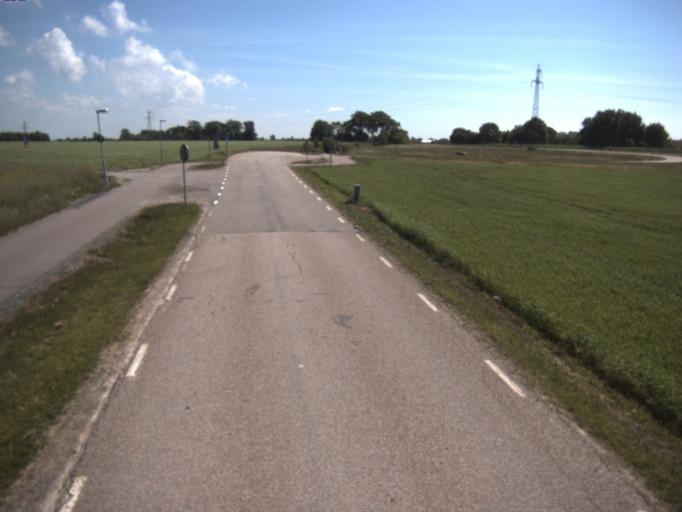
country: SE
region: Skane
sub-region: Helsingborg
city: Barslov
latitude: 56.0166
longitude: 12.8071
